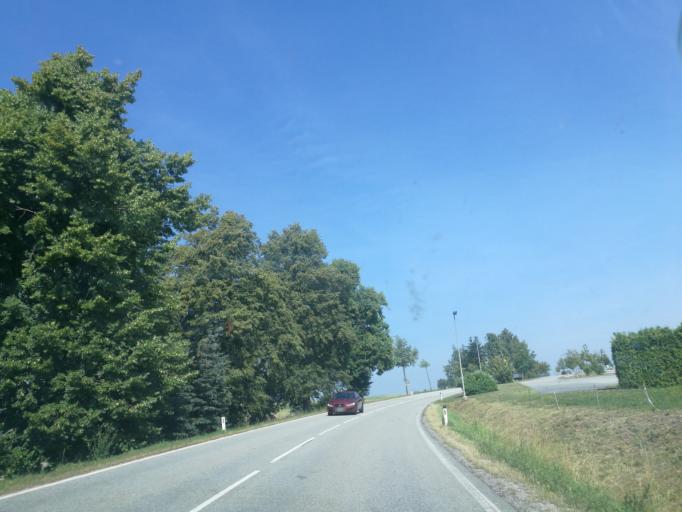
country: AT
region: Lower Austria
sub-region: Politischer Bezirk Gmund
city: Heidenreichstein
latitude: 48.8721
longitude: 15.1183
